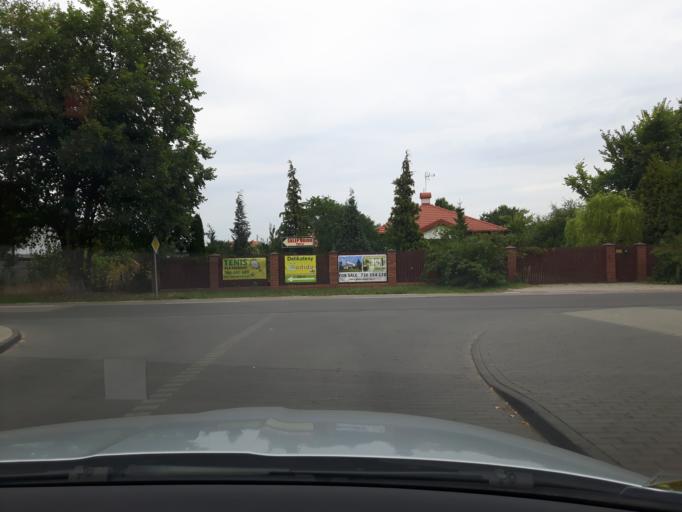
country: PL
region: Masovian Voivodeship
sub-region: Powiat legionowski
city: Wieliszew
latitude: 52.4860
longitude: 20.9704
